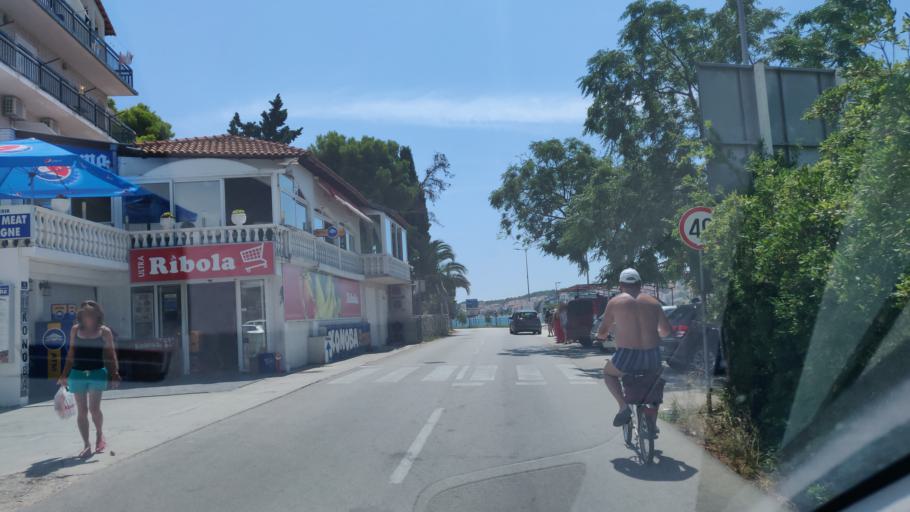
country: HR
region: Splitsko-Dalmatinska
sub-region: Grad Trogir
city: Trogir
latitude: 43.5043
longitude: 16.2581
